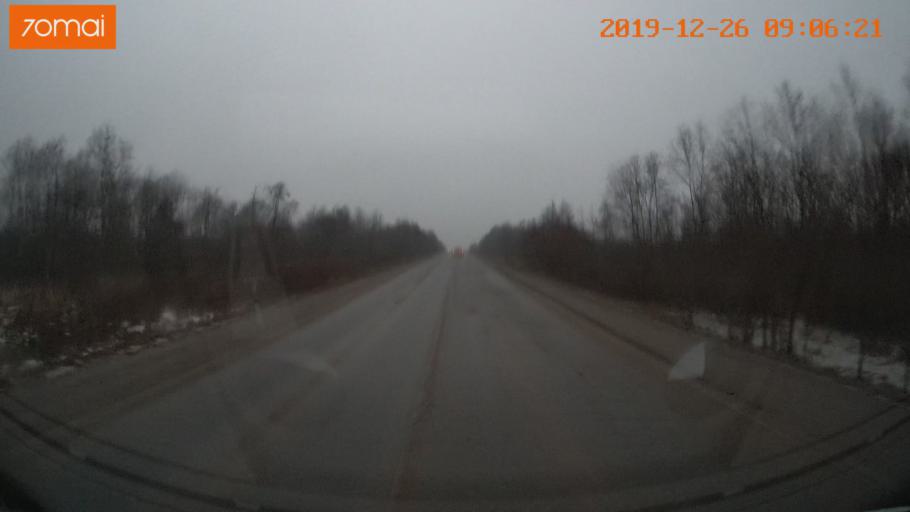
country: RU
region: Vologda
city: Gryazovets
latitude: 58.8352
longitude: 40.2536
